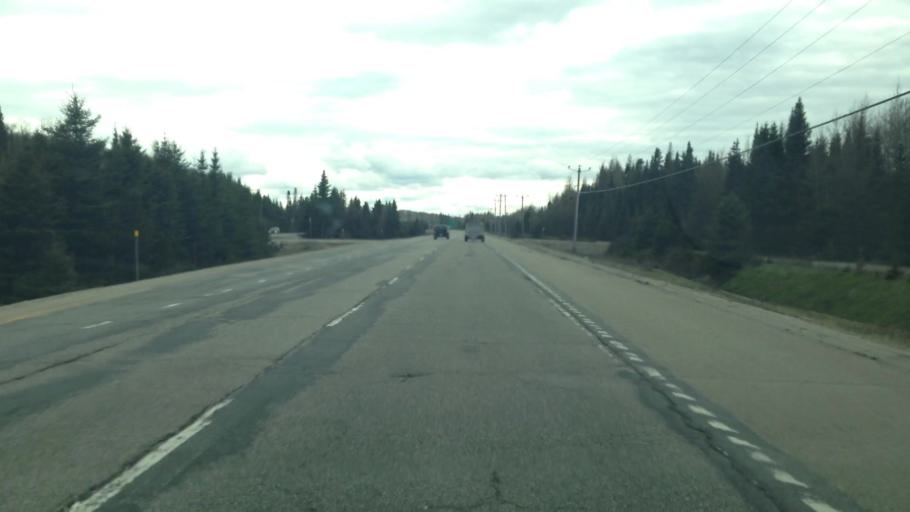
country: CA
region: Quebec
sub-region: Laurentides
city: Mont-Tremblant
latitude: 46.1246
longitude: -74.4406
